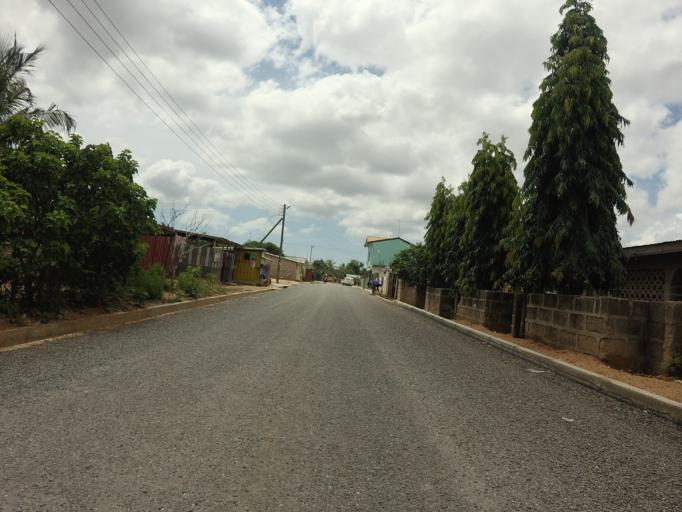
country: GH
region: Central
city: Kasoa
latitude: 5.5468
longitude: -0.3992
